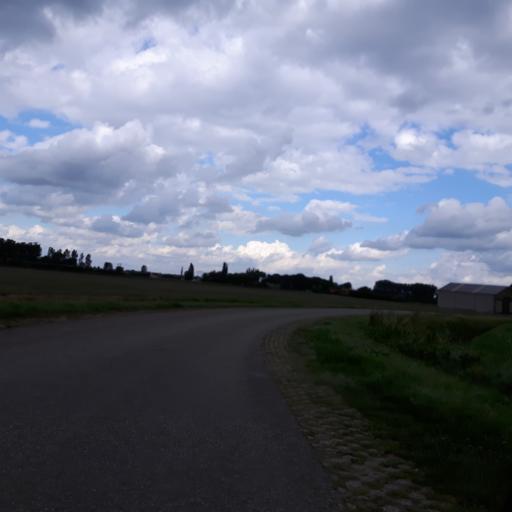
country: NL
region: Zeeland
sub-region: Gemeente Goes
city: Goes
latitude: 51.4953
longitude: 3.8410
